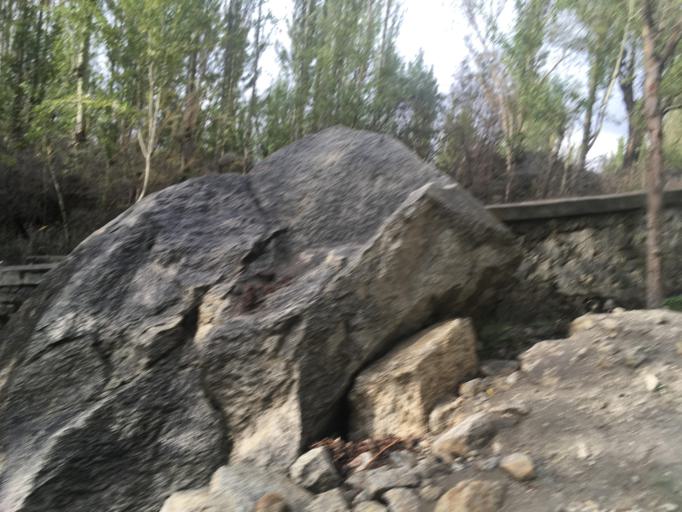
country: PK
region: Gilgit-Baltistan
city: Skardu
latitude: 35.2893
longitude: 75.7049
